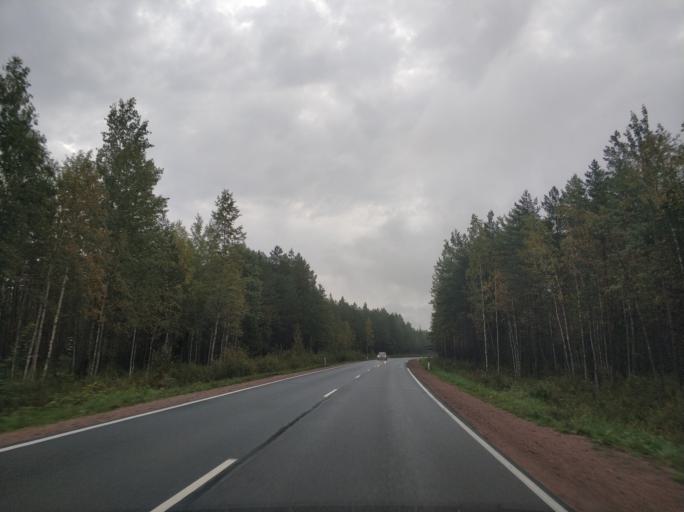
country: RU
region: Leningrad
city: Shcheglovo
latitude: 60.1030
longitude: 30.8133
